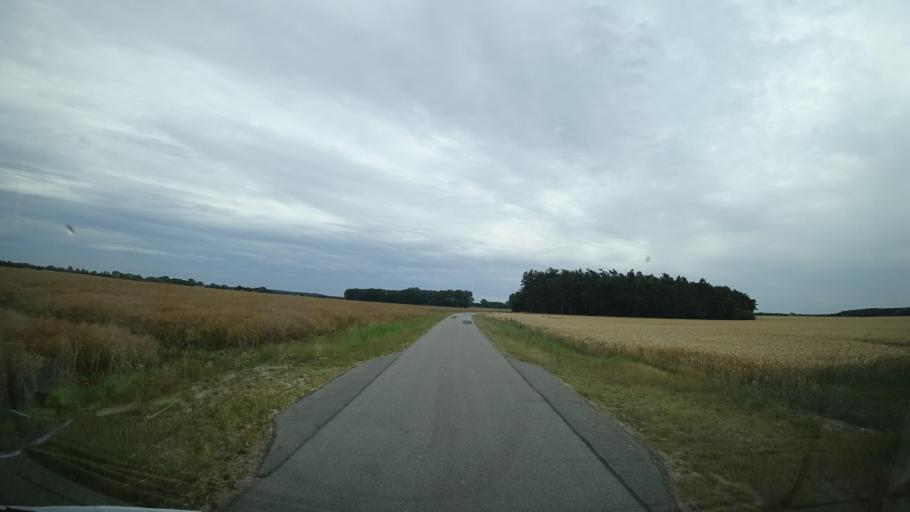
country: DE
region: Mecklenburg-Vorpommern
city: Rambin
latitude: 54.3145
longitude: 13.2063
